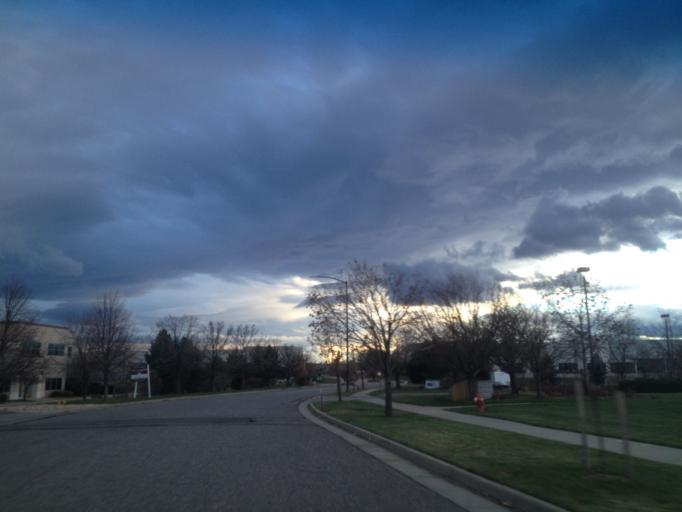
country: US
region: Colorado
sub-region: Boulder County
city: Louisville
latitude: 39.9665
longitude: -105.1126
